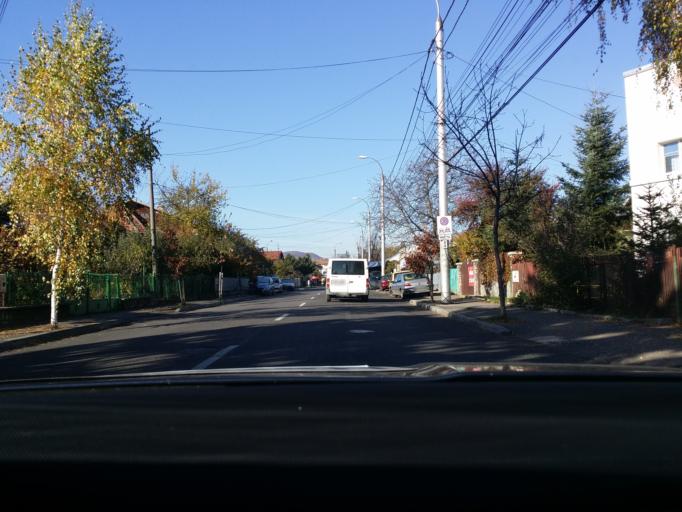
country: RO
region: Prahova
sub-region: Municipiul Campina
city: Campina
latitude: 45.1345
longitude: 25.7316
